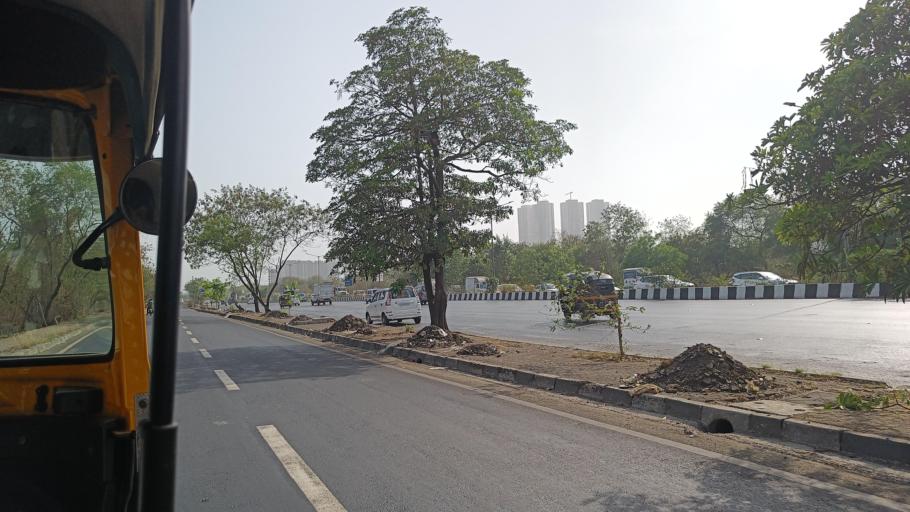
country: IN
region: Maharashtra
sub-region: Mumbai Suburban
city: Powai
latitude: 19.1386
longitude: 72.9472
